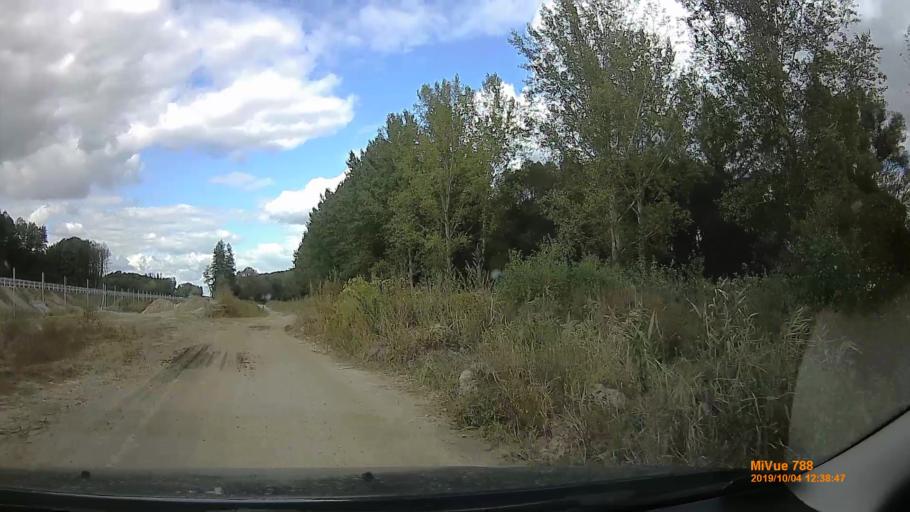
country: HU
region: Somogy
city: Karad
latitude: 46.6692
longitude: 17.7818
